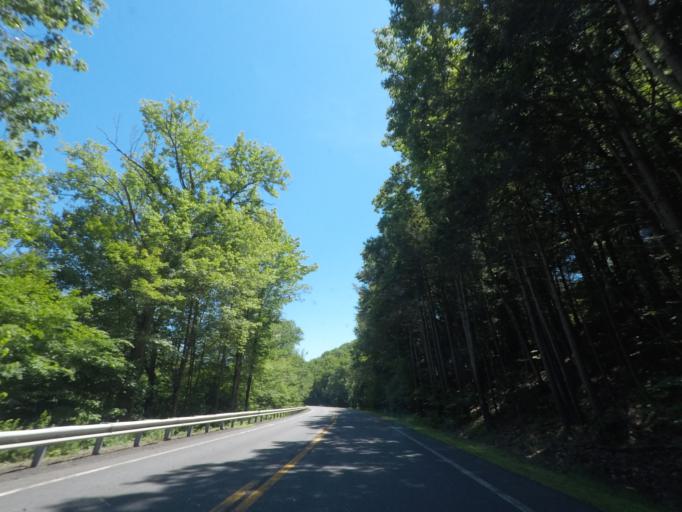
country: US
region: Massachusetts
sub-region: Hampshire County
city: Westhampton
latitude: 42.2414
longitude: -72.9139
